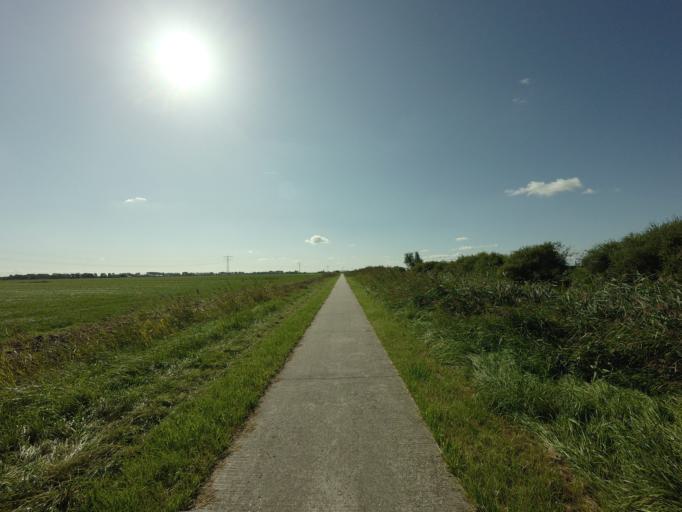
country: NL
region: Friesland
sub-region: Gemeente Boarnsterhim
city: Reduzum
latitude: 53.1477
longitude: 5.7637
